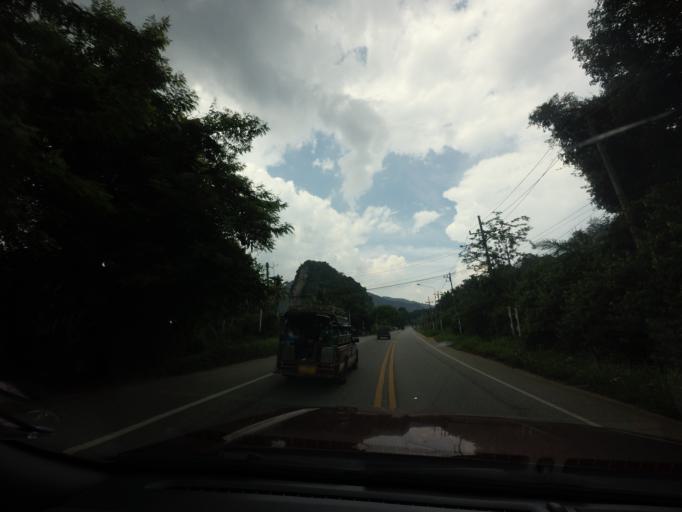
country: TH
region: Yala
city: Than To
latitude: 6.2363
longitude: 101.1703
